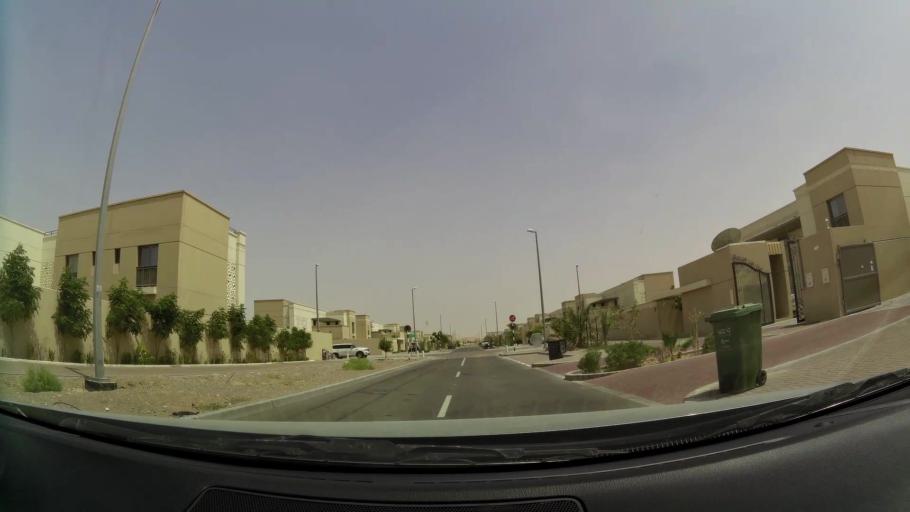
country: AE
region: Abu Dhabi
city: Al Ain
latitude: 24.1459
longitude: 55.6226
